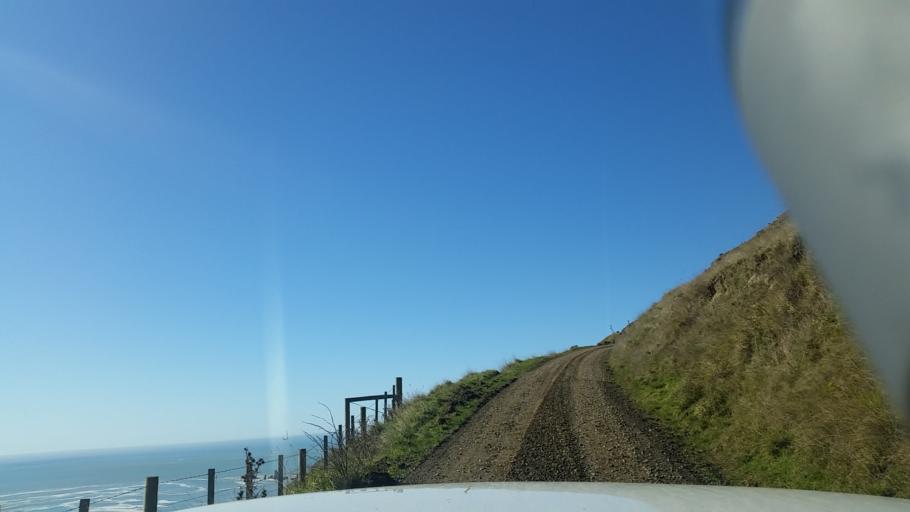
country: NZ
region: Canterbury
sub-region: Christchurch City
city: Christchurch
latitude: -43.6632
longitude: 172.9876
